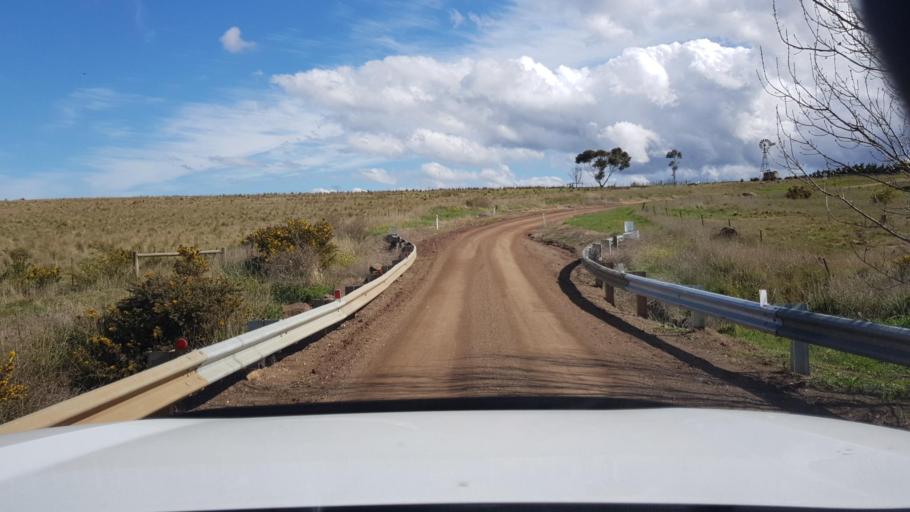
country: AU
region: Victoria
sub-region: Hume
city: Sunbury
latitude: -37.5826
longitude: 144.6315
